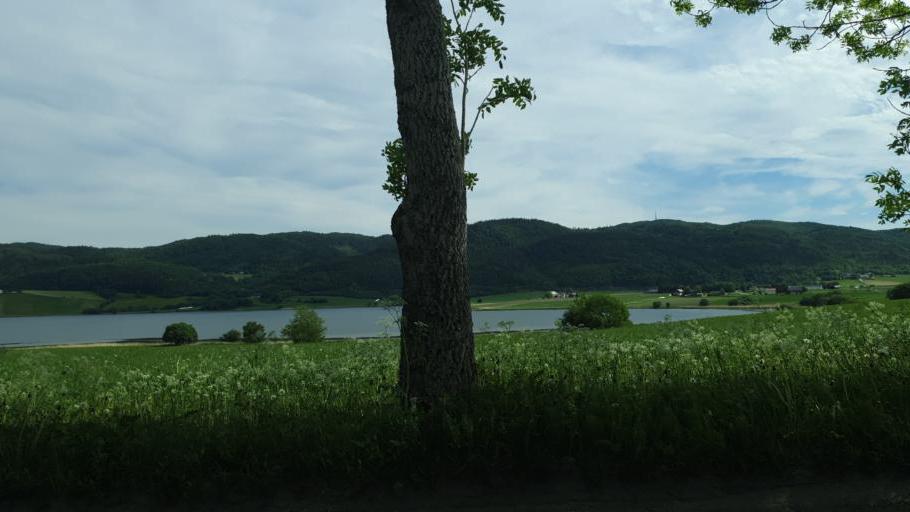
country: NO
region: Sor-Trondelag
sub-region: Rissa
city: Rissa
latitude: 63.5670
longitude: 9.9294
